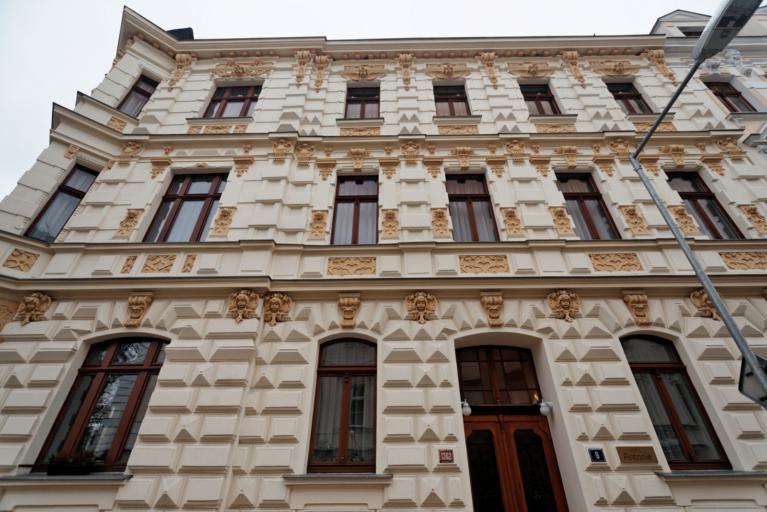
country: CZ
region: Ustecky
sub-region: Okres Teplice
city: Teplice
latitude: 50.6423
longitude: 13.8398
